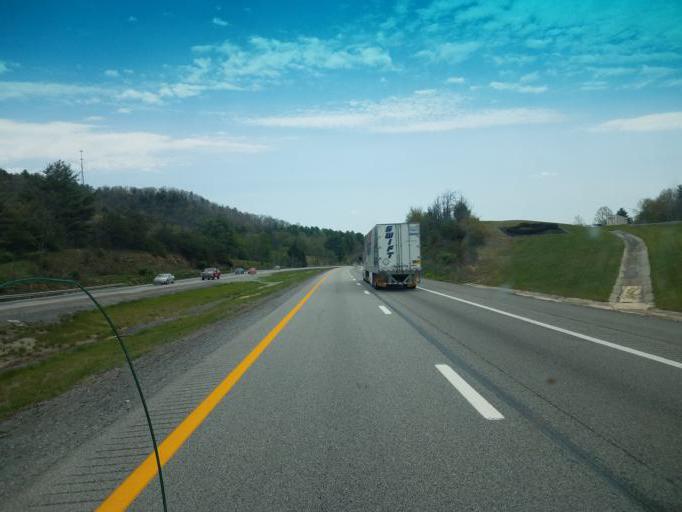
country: US
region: West Virginia
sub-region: Mercer County
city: Athens
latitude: 37.4877
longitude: -81.0822
